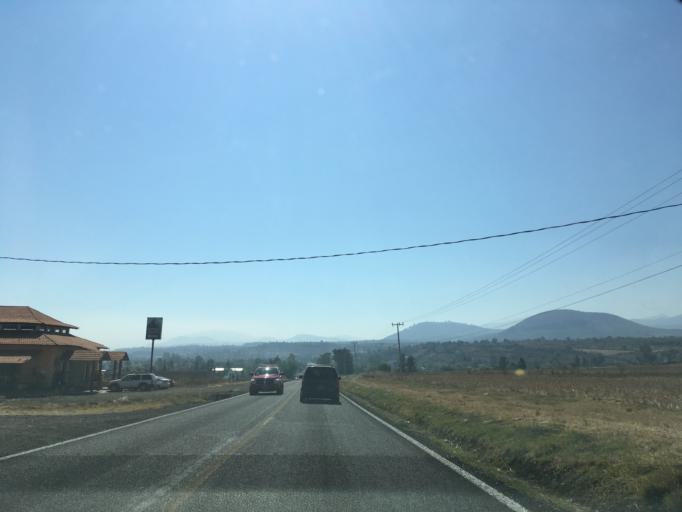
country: MX
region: Michoacan
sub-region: Indaparapeo
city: San Lucas Pio
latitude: 19.7955
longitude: -100.9395
